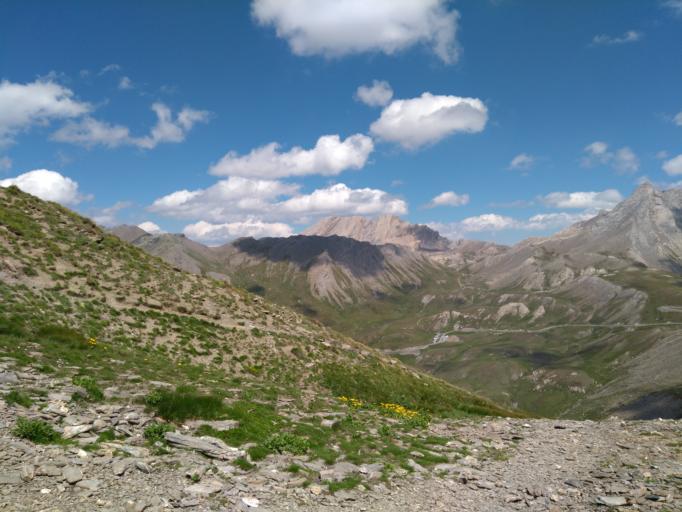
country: IT
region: Piedmont
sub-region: Provincia di Cuneo
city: Pontechianale
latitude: 44.6814
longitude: 6.9606
